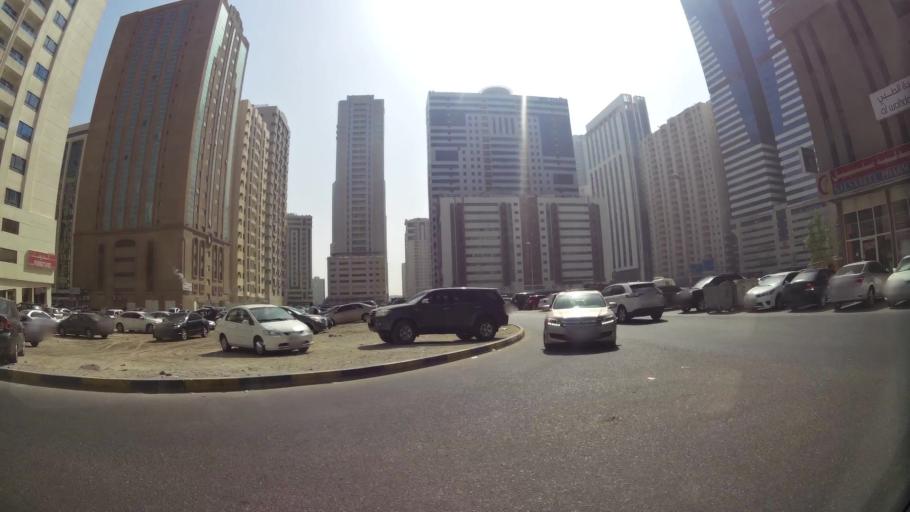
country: AE
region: Ash Shariqah
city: Sharjah
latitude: 25.3008
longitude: 55.3779
